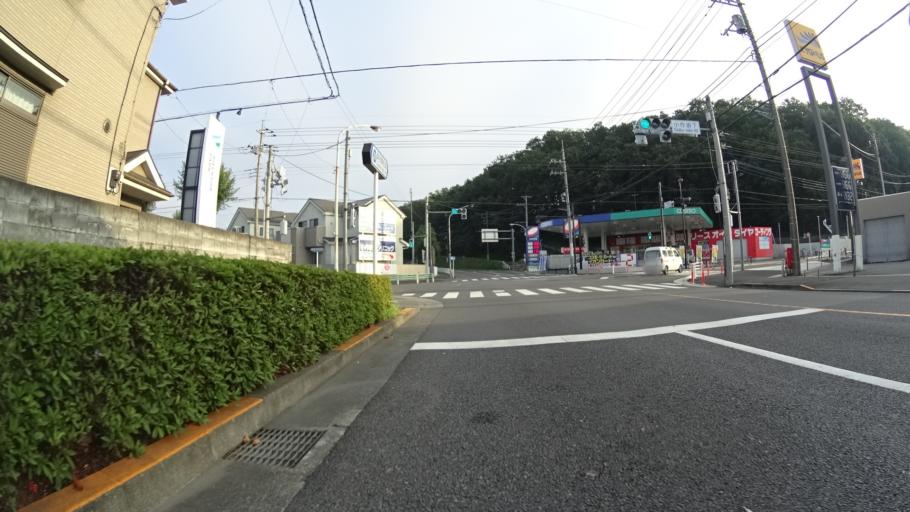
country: JP
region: Tokyo
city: Fussa
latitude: 35.7717
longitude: 139.2979
